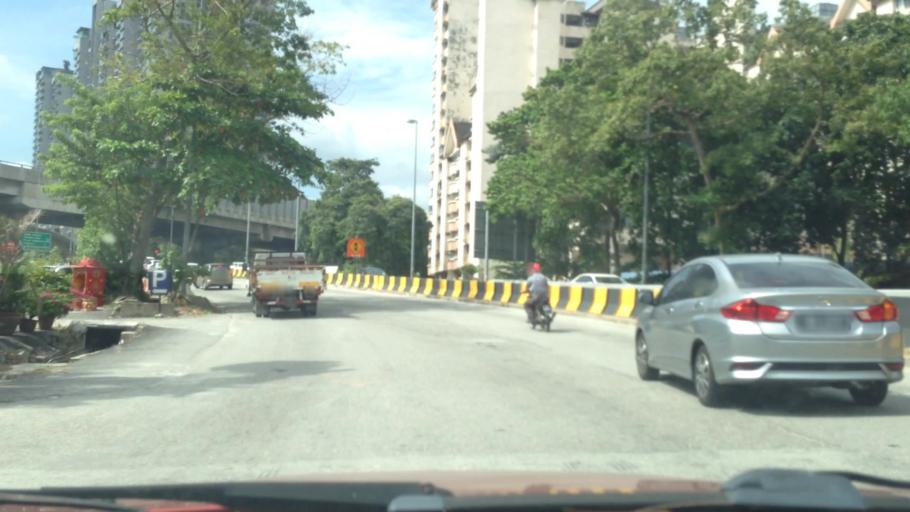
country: MY
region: Kuala Lumpur
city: Kuala Lumpur
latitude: 3.0880
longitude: 101.6932
